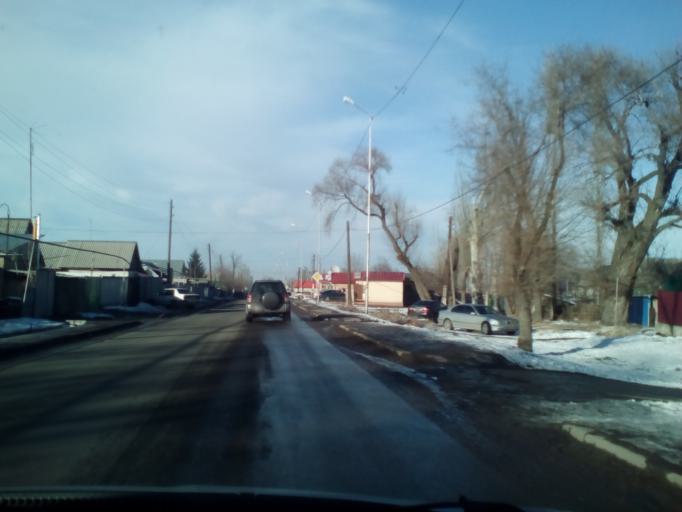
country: KZ
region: Almaty Oblysy
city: Burunday
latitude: 43.1711
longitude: 76.4159
